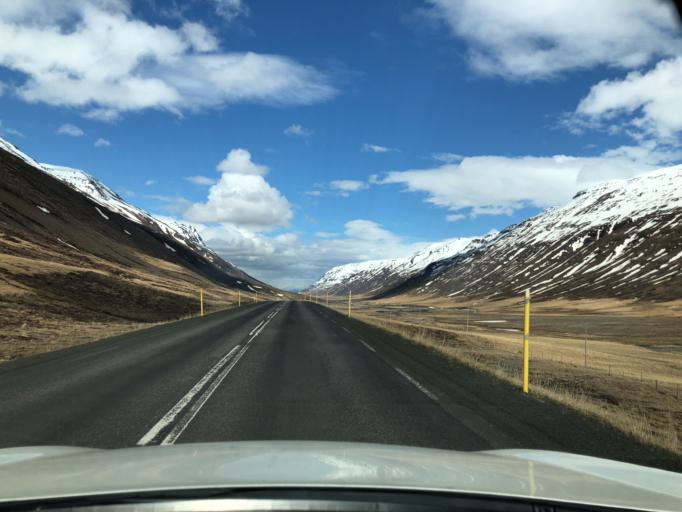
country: IS
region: Northeast
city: Dalvik
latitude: 65.4846
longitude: -18.6502
